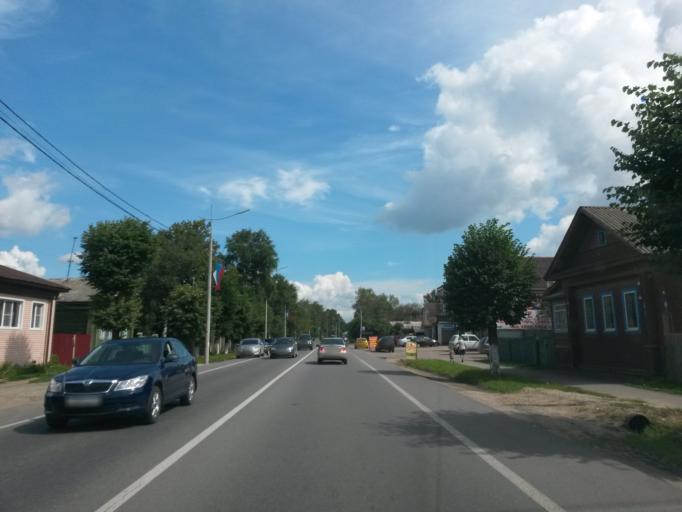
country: RU
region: Jaroslavl
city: Pereslavl'-Zalesskiy
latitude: 56.7261
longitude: 38.8399
